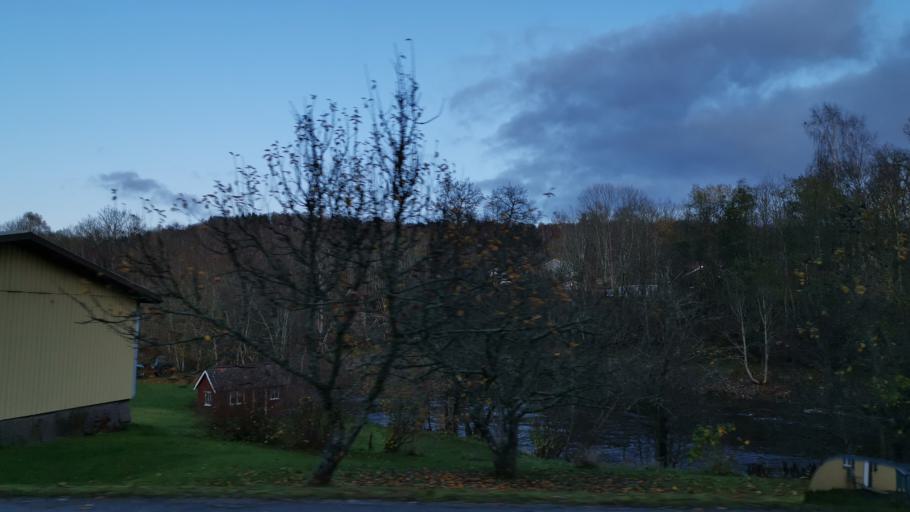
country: SE
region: Vaestra Goetaland
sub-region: Munkedals Kommun
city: Munkedal
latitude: 58.4635
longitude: 11.6825
